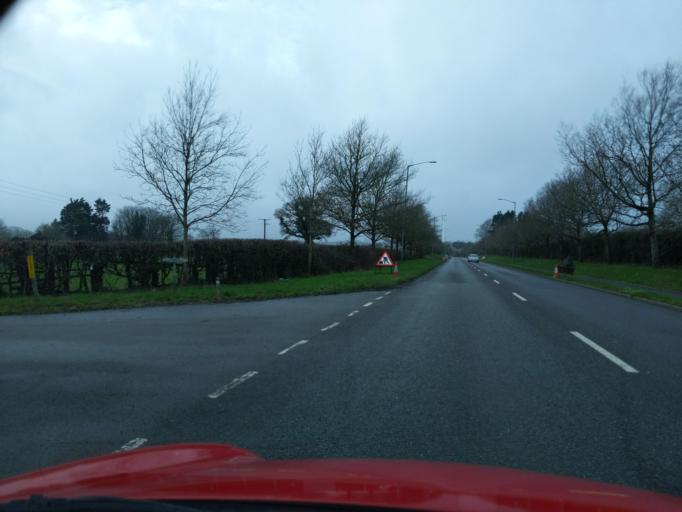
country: GB
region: England
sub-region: Cornwall
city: Launceston
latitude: 50.6264
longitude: -4.3617
